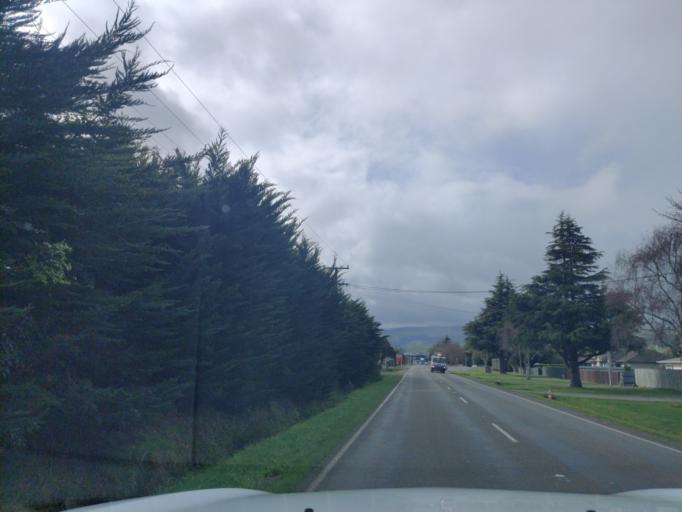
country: NZ
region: Manawatu-Wanganui
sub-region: Palmerston North City
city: Palmerston North
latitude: -40.2948
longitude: 175.7497
